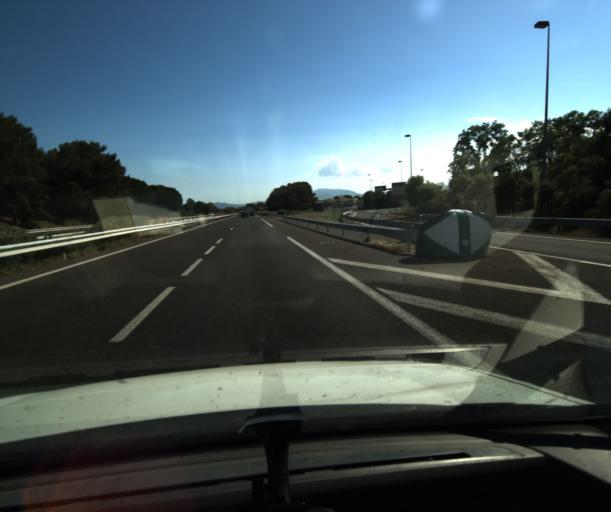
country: FR
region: Languedoc-Roussillon
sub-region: Departement des Pyrenees-Orientales
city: Villemolaque
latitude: 42.5847
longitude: 2.8468
